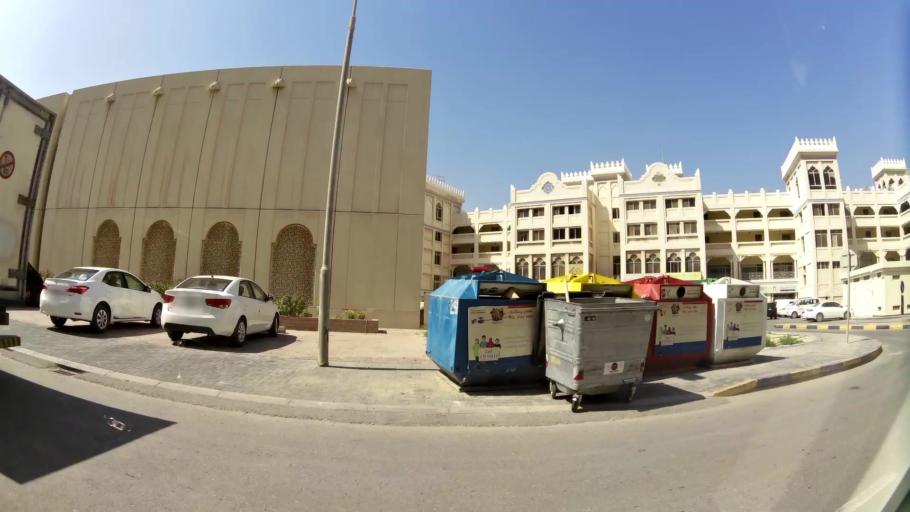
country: BH
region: Manama
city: Manama
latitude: 26.2136
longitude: 50.5979
